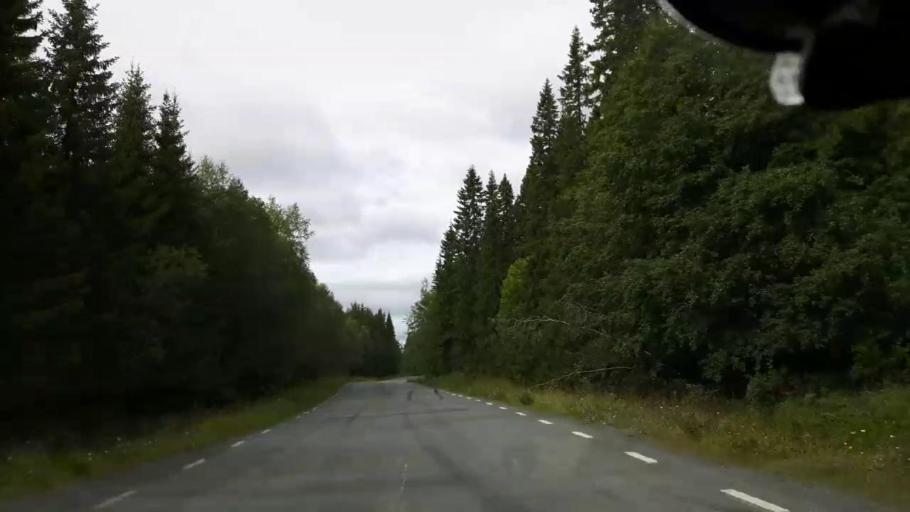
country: SE
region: Jaemtland
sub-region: Krokoms Kommun
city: Valla
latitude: 63.4806
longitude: 13.9406
